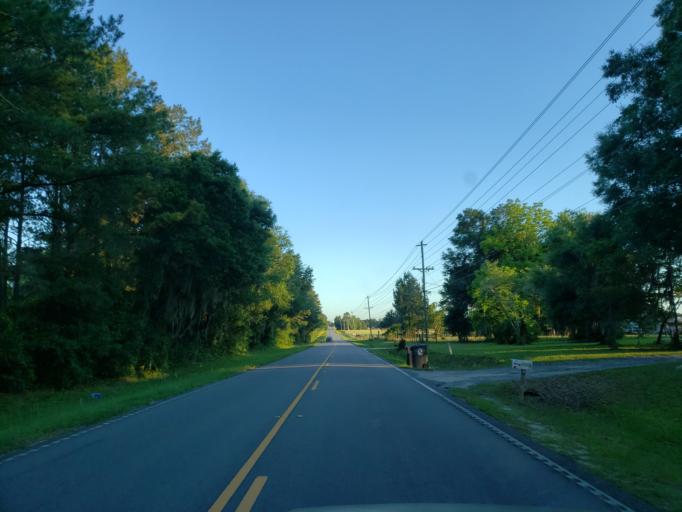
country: US
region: Georgia
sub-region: Lowndes County
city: Valdosta
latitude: 30.7048
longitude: -83.2412
